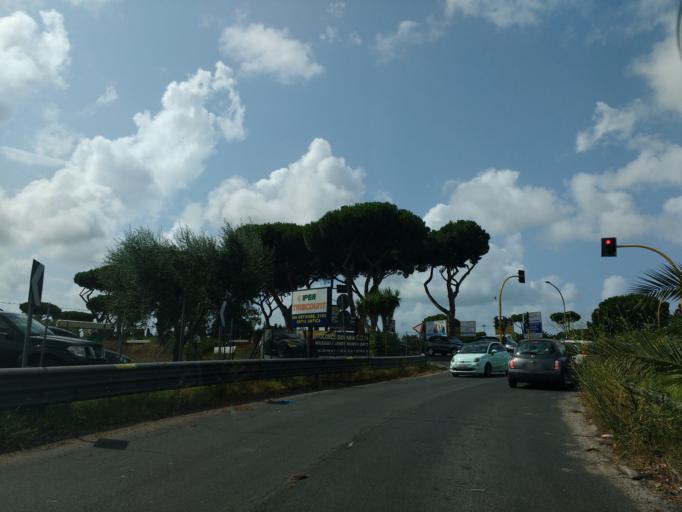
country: IT
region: Latium
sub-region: Citta metropolitana di Roma Capitale
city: Acilia-Castel Fusano-Ostia Antica
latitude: 41.7596
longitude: 12.3045
